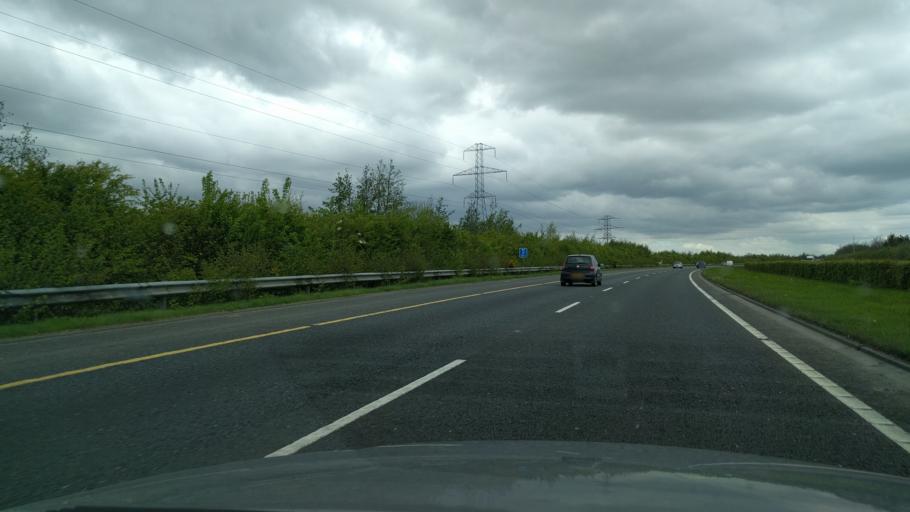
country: IE
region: Leinster
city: Lusk
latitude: 53.5122
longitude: -6.2061
